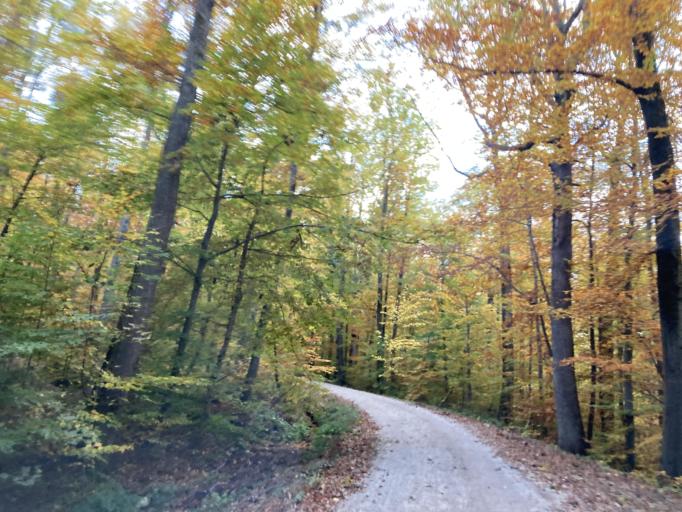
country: DE
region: Baden-Wuerttemberg
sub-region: Tuebingen Region
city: Gomaringen
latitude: 48.4663
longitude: 9.1327
